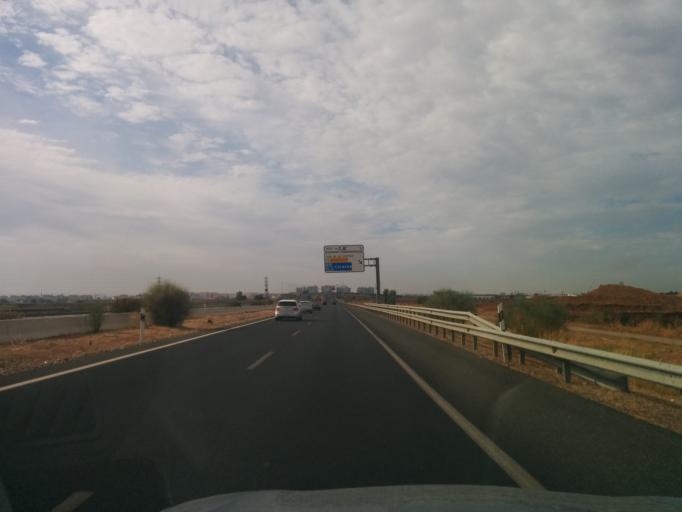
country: ES
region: Andalusia
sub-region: Provincia de Sevilla
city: La Rinconada
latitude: 37.4458
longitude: -5.9714
